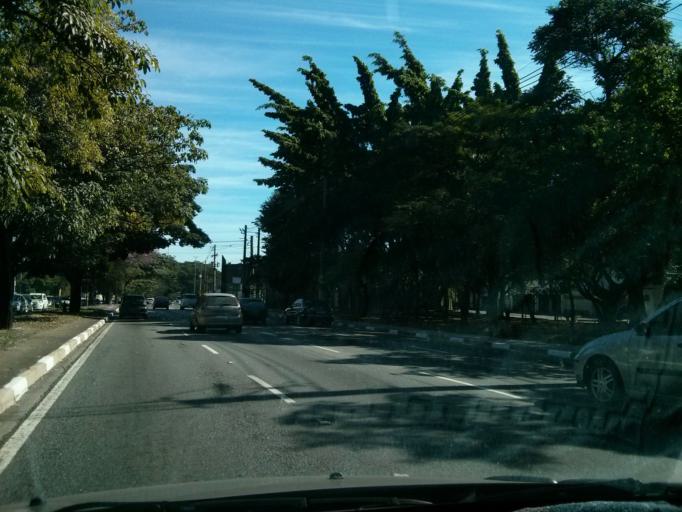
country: BR
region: Sao Paulo
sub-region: Sao Paulo
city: Sao Paulo
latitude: -23.6130
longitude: -46.6706
